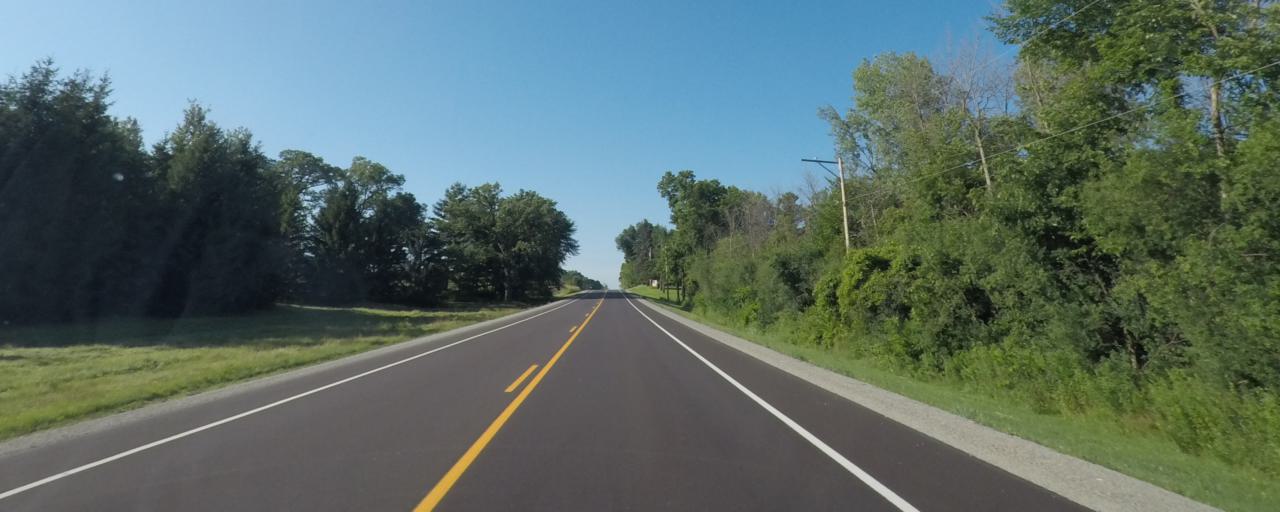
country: US
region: Wisconsin
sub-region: Jefferson County
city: Palmyra
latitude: 42.9294
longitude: -88.5862
